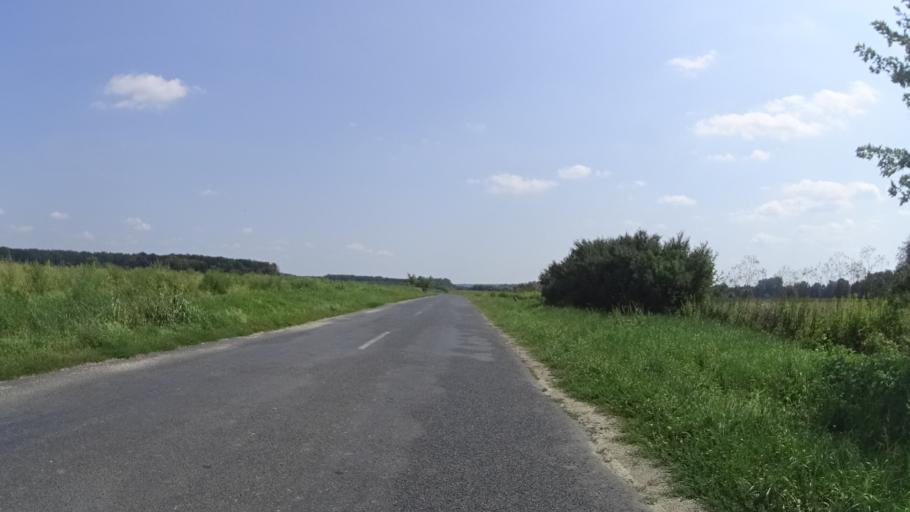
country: HU
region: Zala
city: Murakeresztur
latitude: 46.3752
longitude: 16.8510
